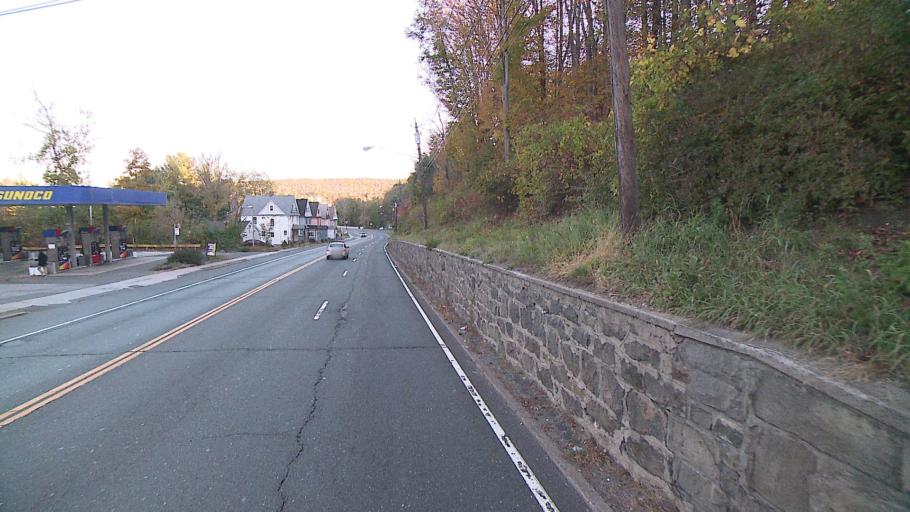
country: US
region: Connecticut
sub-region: Litchfield County
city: Winsted
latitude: 41.9174
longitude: -73.0565
